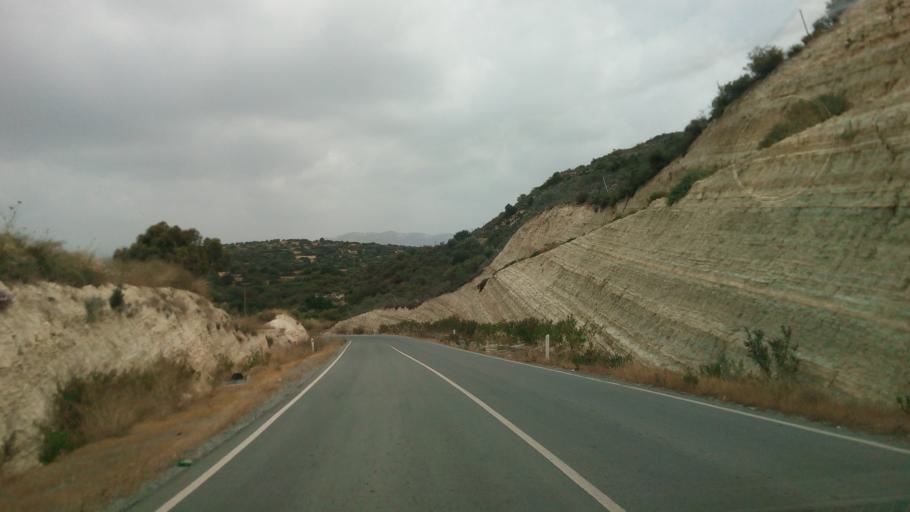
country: CY
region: Limassol
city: Pano Polemidia
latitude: 34.7461
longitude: 32.9545
